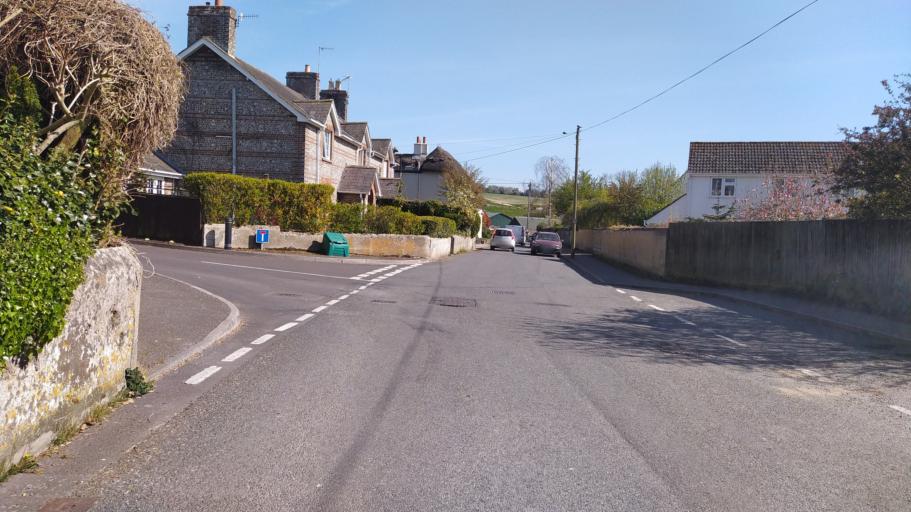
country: GB
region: England
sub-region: Dorset
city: Blandford Forum
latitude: 50.8833
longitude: -2.1353
